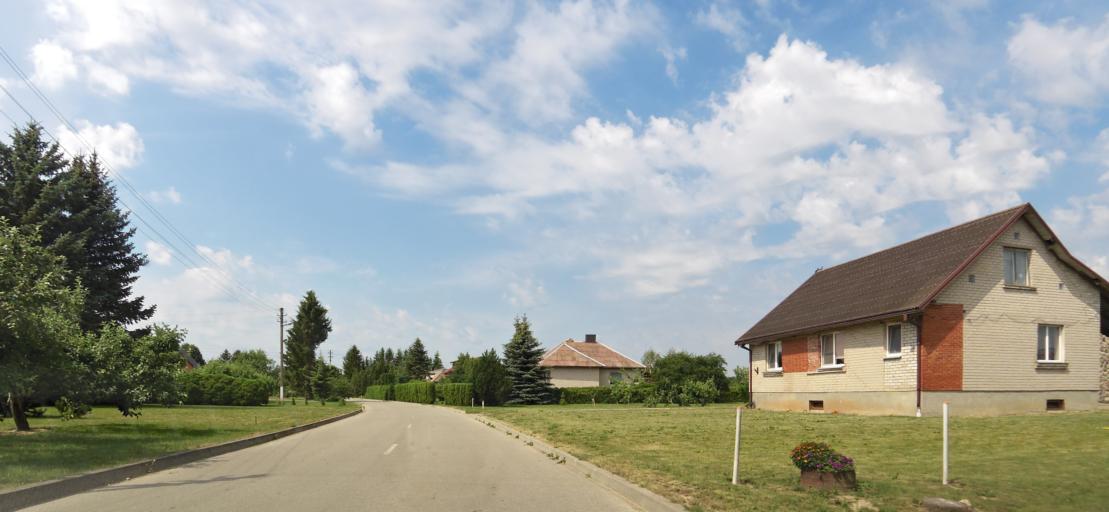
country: LT
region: Panevezys
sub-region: Birzai
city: Birzai
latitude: 56.2673
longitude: 24.6123
